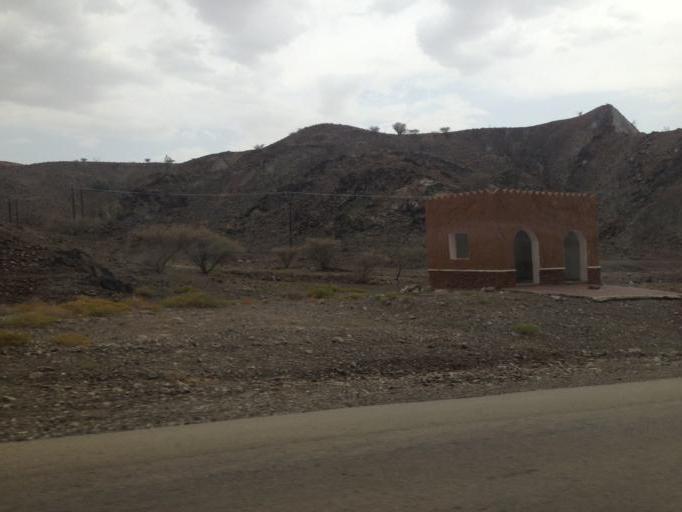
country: OM
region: Ash Sharqiyah
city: Badiyah
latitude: 22.5623
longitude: 59.0309
